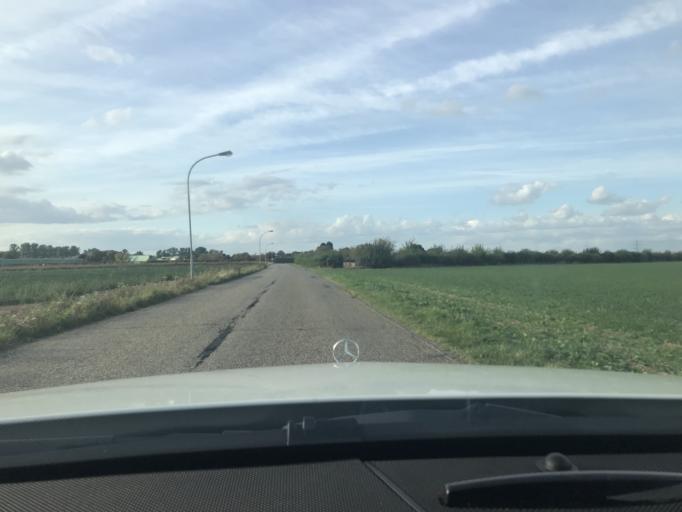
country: DE
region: North Rhine-Westphalia
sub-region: Regierungsbezirk Dusseldorf
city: Neubrueck
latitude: 51.1266
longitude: 6.6812
